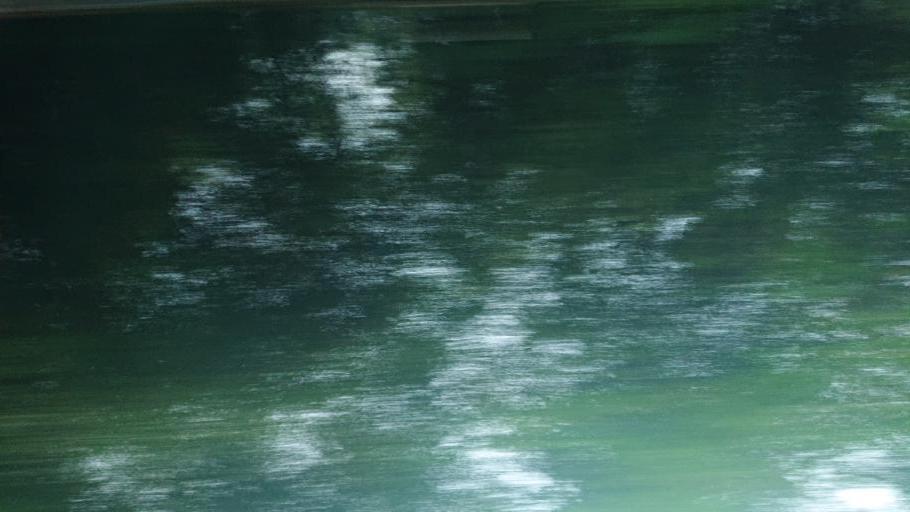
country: TW
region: Taiwan
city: Lugu
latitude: 23.5138
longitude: 120.7021
